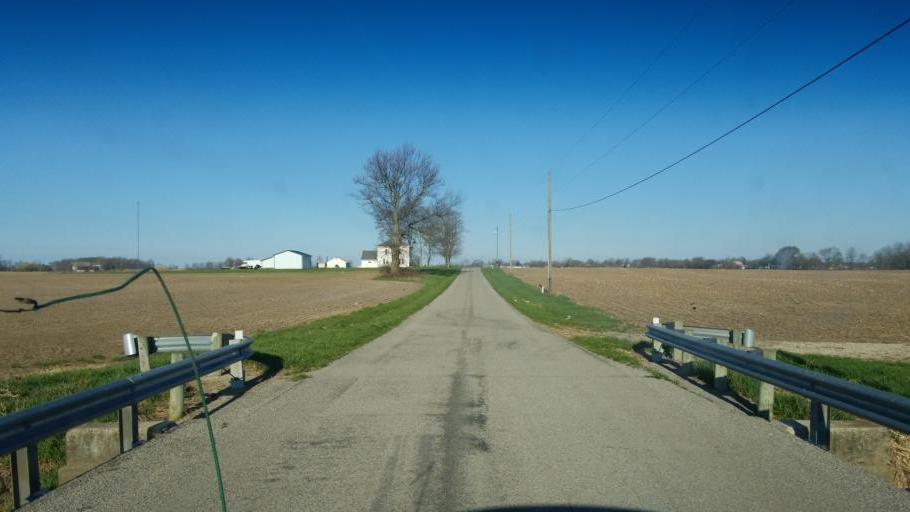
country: US
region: Ohio
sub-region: Union County
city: Richwood
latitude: 40.4513
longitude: -83.4398
